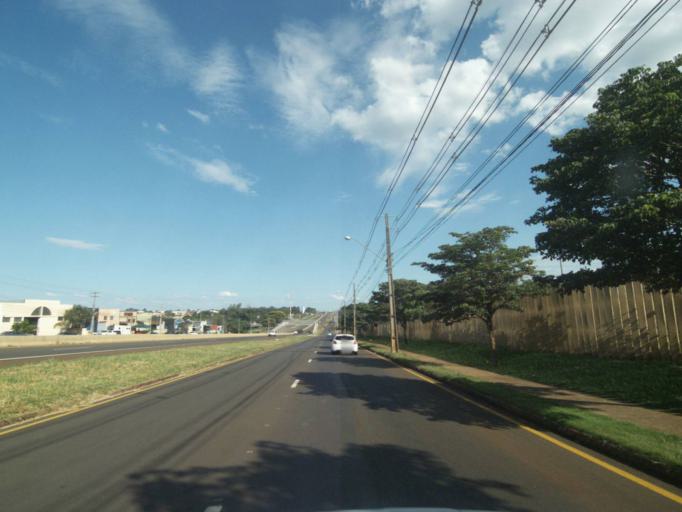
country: BR
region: Parana
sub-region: Londrina
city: Londrina
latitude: -23.3524
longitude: -51.1639
